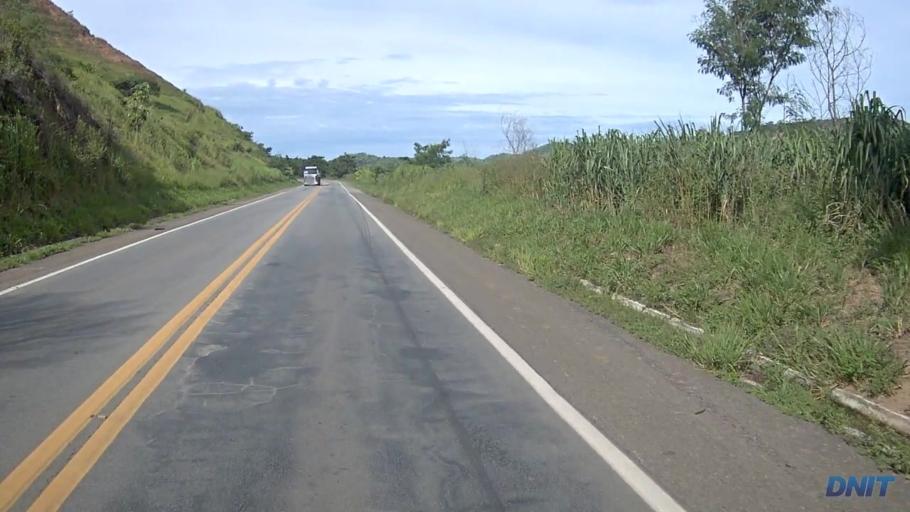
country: BR
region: Minas Gerais
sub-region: Belo Oriente
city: Belo Oriente
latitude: -19.1727
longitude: -42.2520
